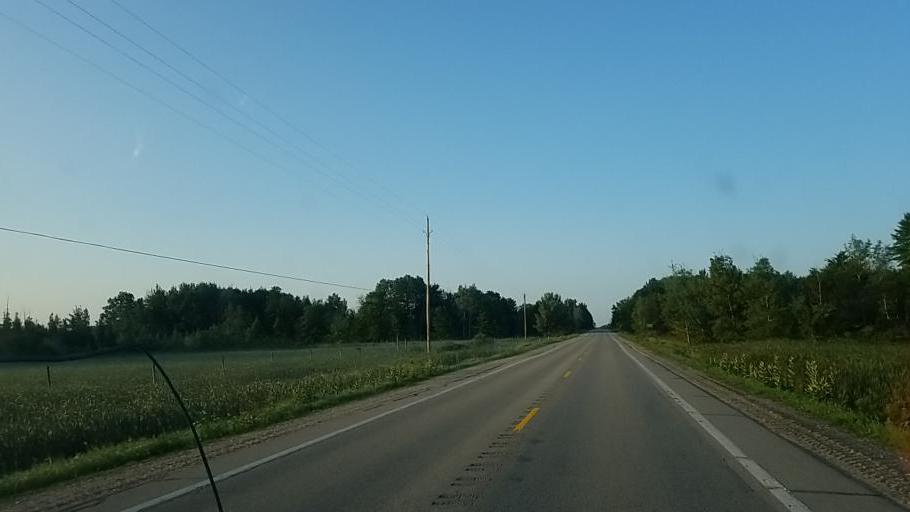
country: US
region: Michigan
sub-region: Isabella County
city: Lake Isabella
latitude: 43.6389
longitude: -85.1461
